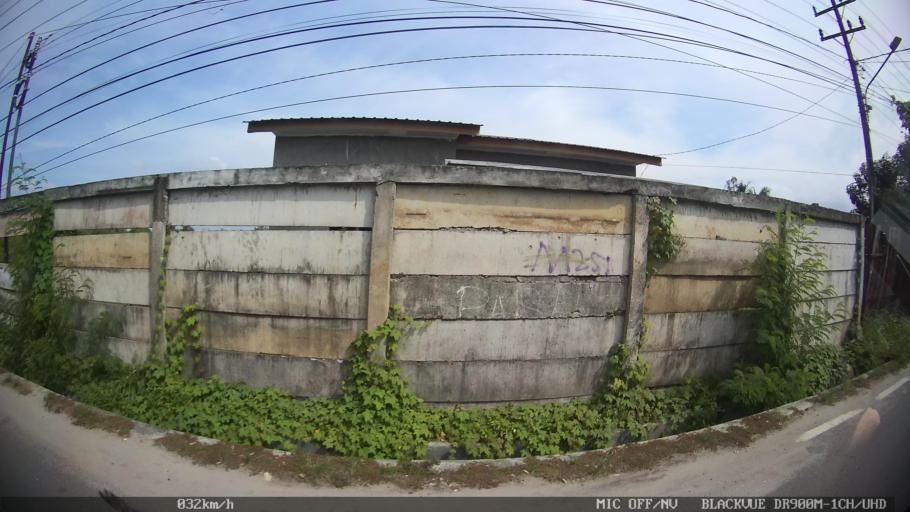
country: ID
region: North Sumatra
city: Percut
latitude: 3.6096
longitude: 98.7975
